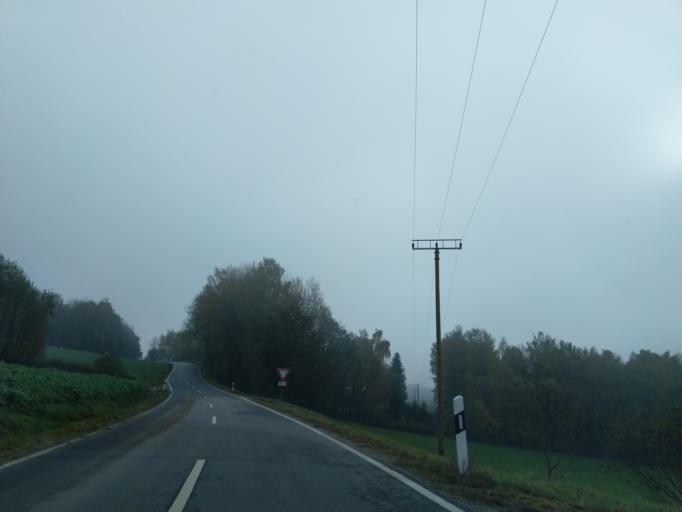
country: DE
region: Bavaria
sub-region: Lower Bavaria
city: Grattersdorf
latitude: 48.7905
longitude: 13.1559
